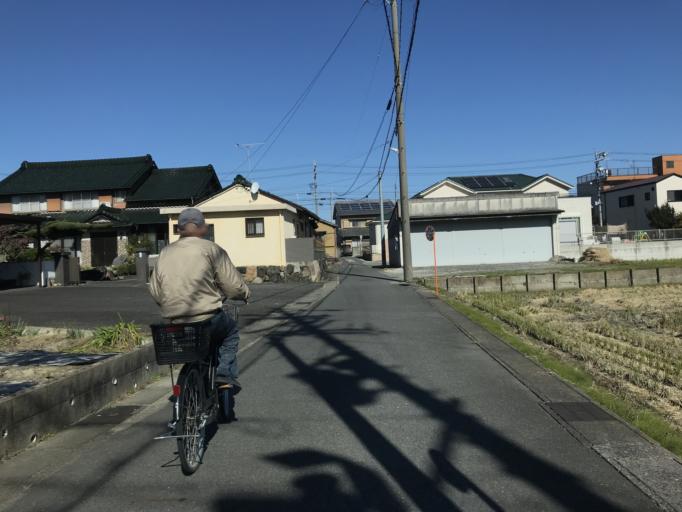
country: JP
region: Aichi
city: Kanie
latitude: 35.1541
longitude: 136.7971
